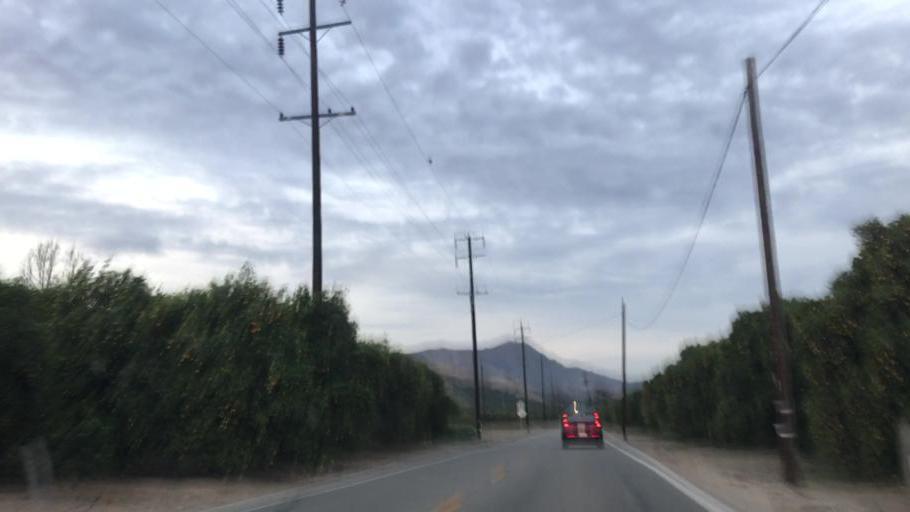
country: US
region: California
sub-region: Ventura County
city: Fillmore
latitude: 34.3630
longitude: -118.9469
